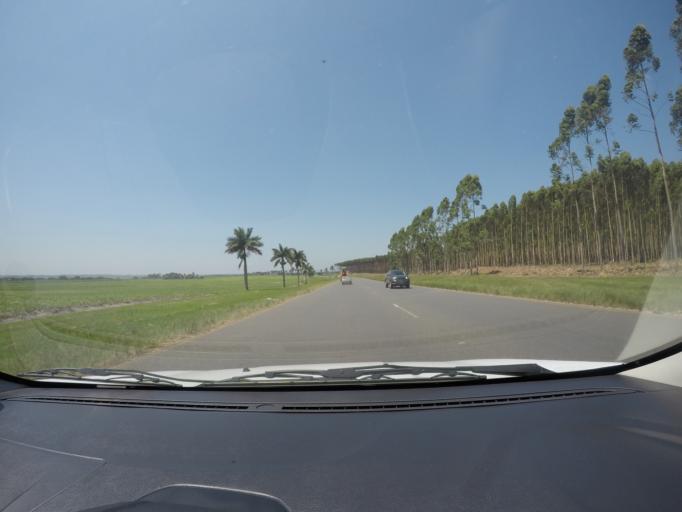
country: ZA
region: KwaZulu-Natal
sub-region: uThungulu District Municipality
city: eSikhawini
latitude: -28.8179
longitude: 31.9522
